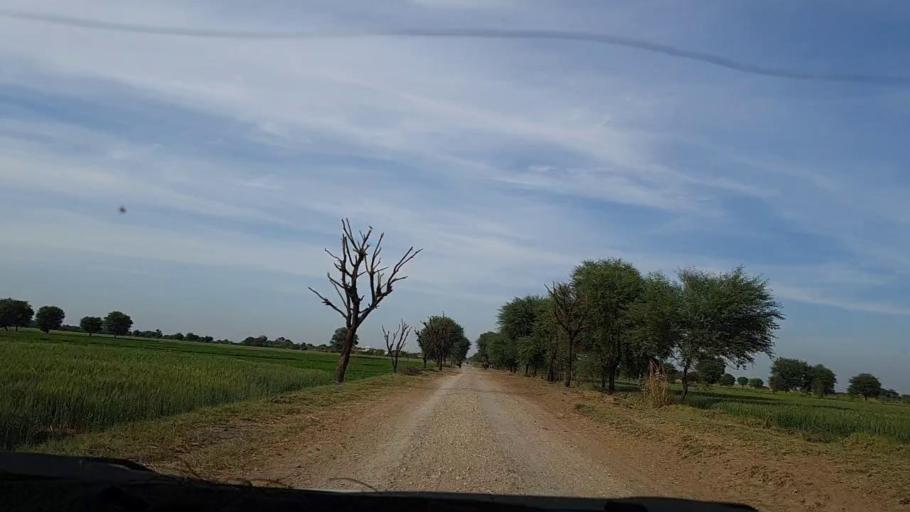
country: PK
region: Sindh
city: Dhoro Naro
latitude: 25.4429
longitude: 69.5123
